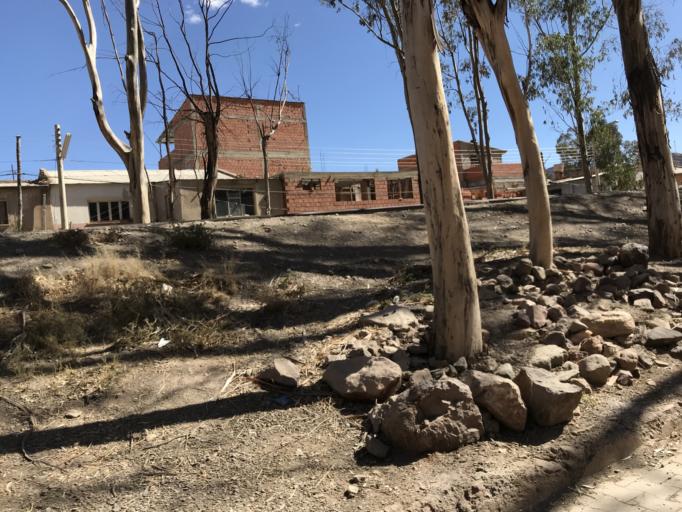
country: BO
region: Potosi
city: Tupiza
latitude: -21.4460
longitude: -65.7158
